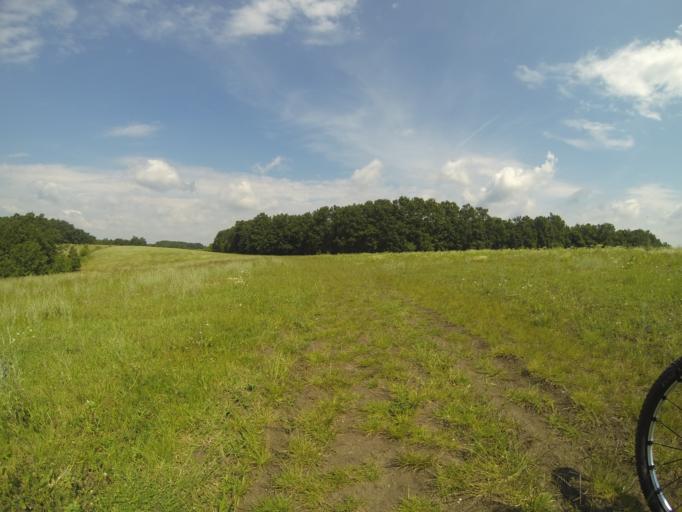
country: RO
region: Gorj
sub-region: Comuna Stoina
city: Stoina
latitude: 44.6316
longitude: 23.6093
